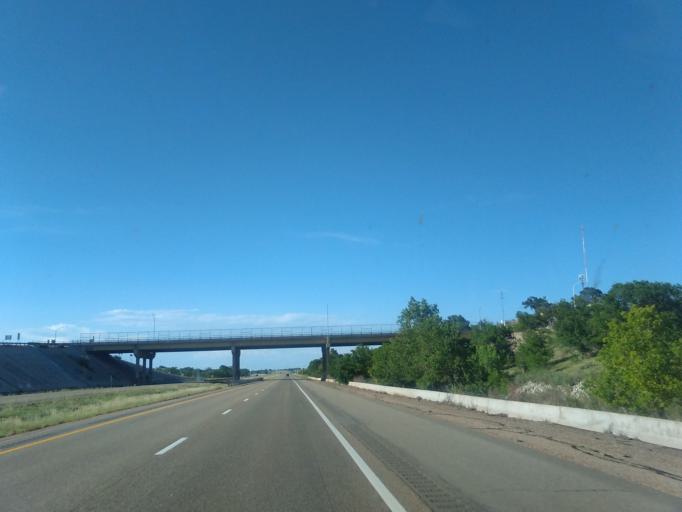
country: US
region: New Mexico
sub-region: San Miguel County
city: Las Vegas
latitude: 35.5941
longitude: -105.2093
